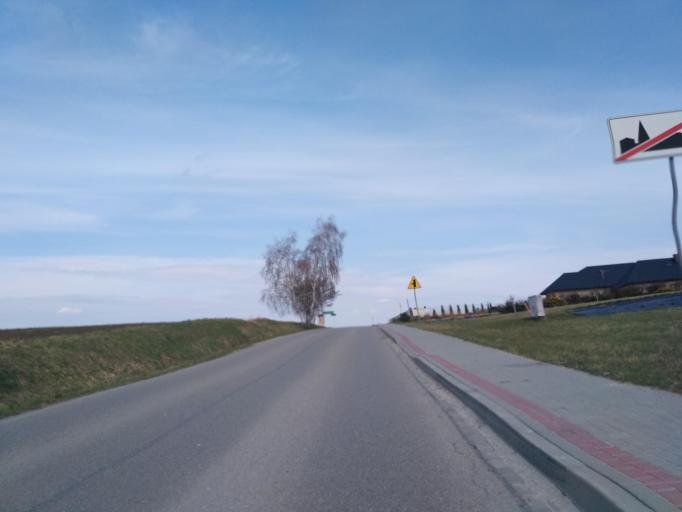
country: PL
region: Subcarpathian Voivodeship
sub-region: Powiat rzeszowski
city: Zglobien
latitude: 49.9937
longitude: 21.8021
